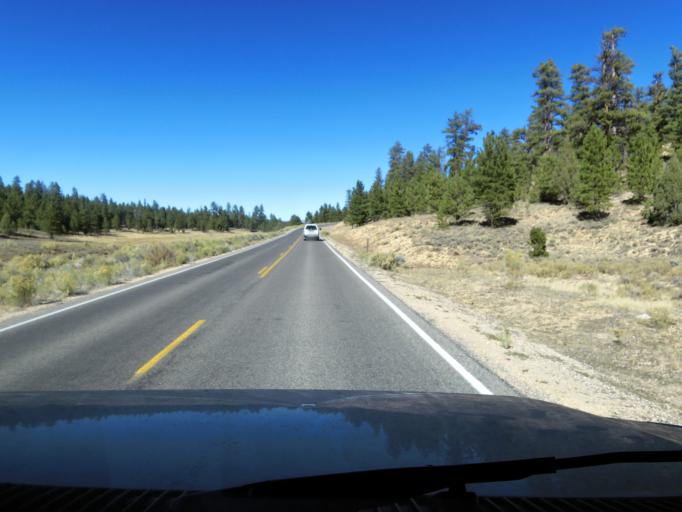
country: US
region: Utah
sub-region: Garfield County
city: Panguitch
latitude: 37.6000
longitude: -112.2080
